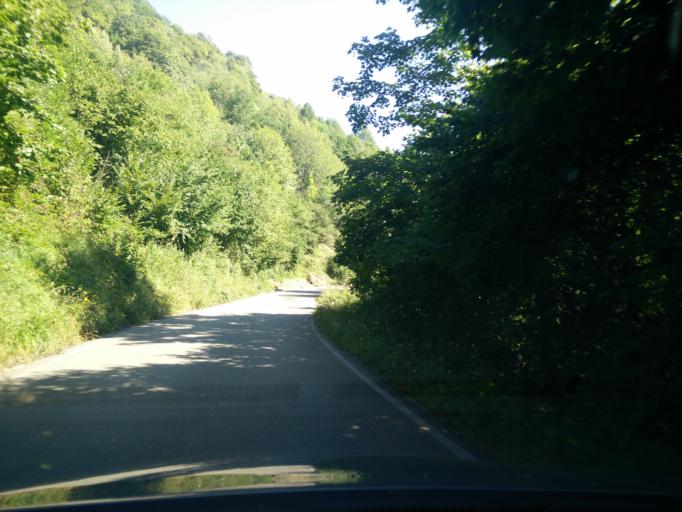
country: ES
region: Asturias
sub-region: Province of Asturias
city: Campo de Caso
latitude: 43.1842
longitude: -5.3879
